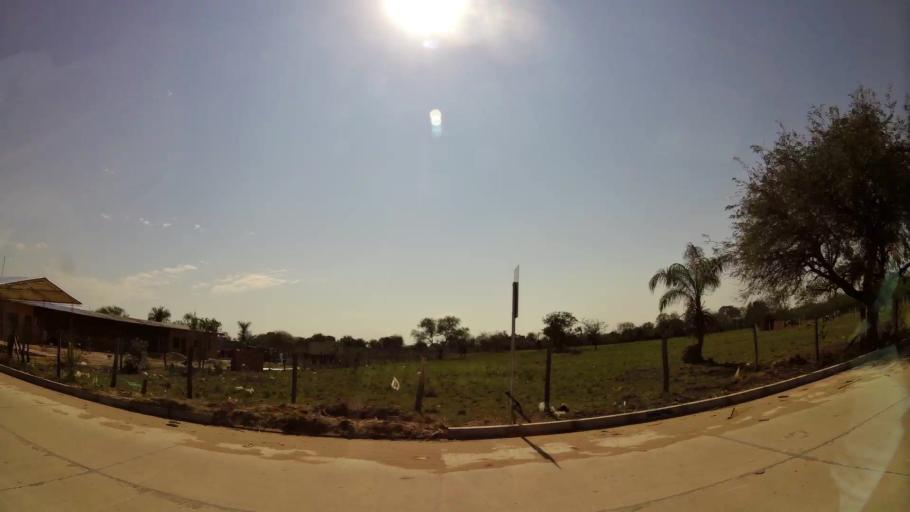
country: BO
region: Santa Cruz
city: Cotoca
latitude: -17.7128
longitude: -63.0666
